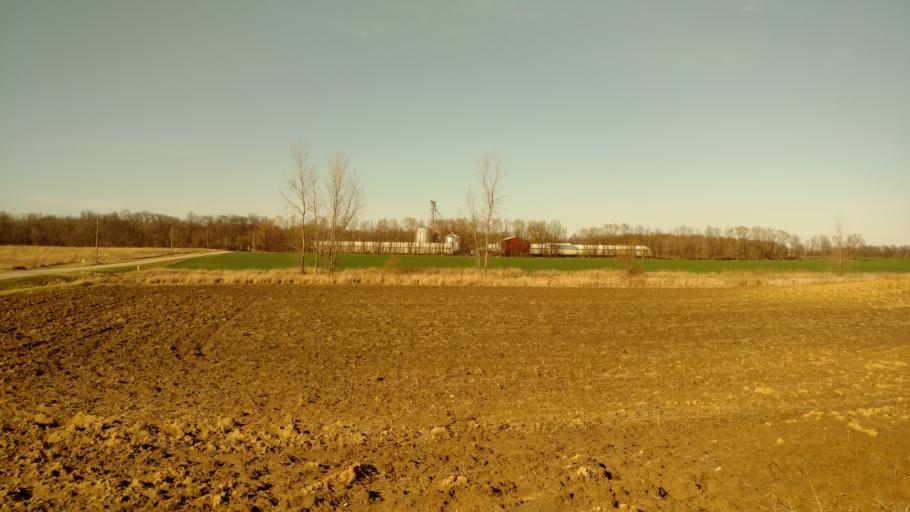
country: US
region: Ohio
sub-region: Crawford County
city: Bucyrus
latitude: 40.7044
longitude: -82.9386
